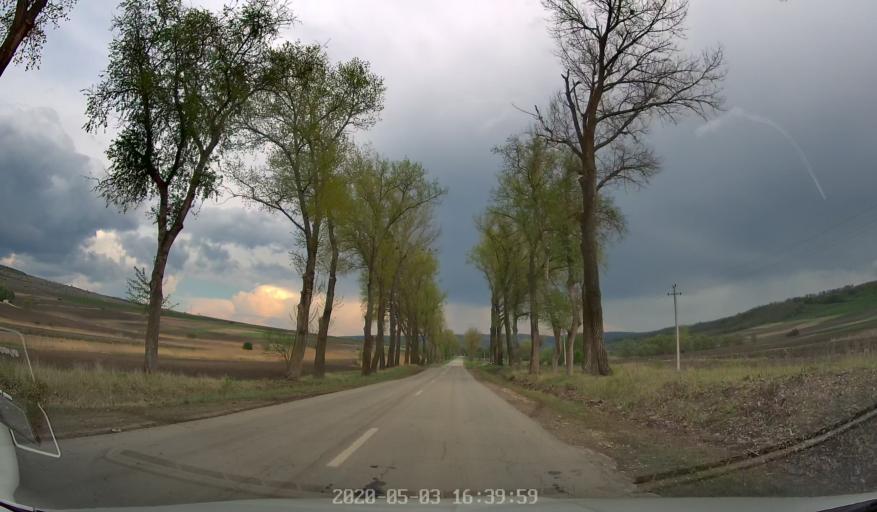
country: MD
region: Stinga Nistrului
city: Bucovat
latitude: 47.1786
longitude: 28.3841
